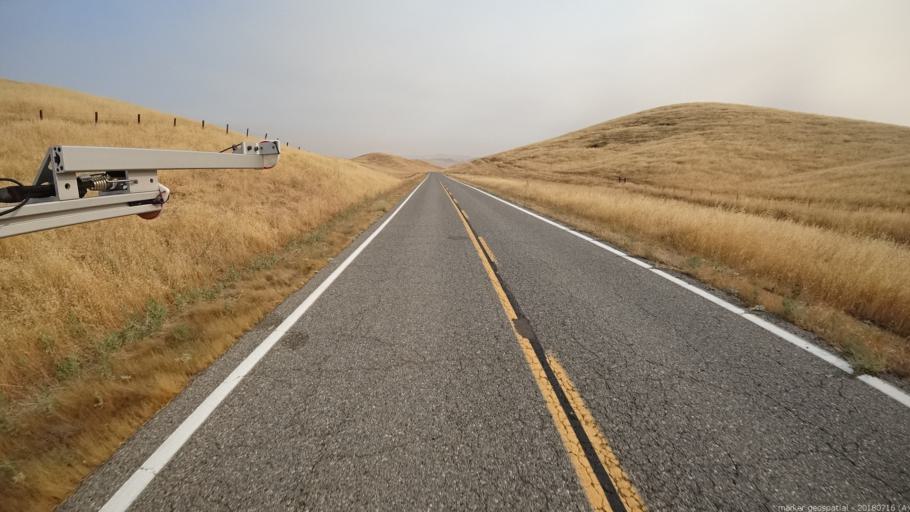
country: US
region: California
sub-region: Madera County
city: Madera Acres
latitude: 37.1819
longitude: -120.0019
